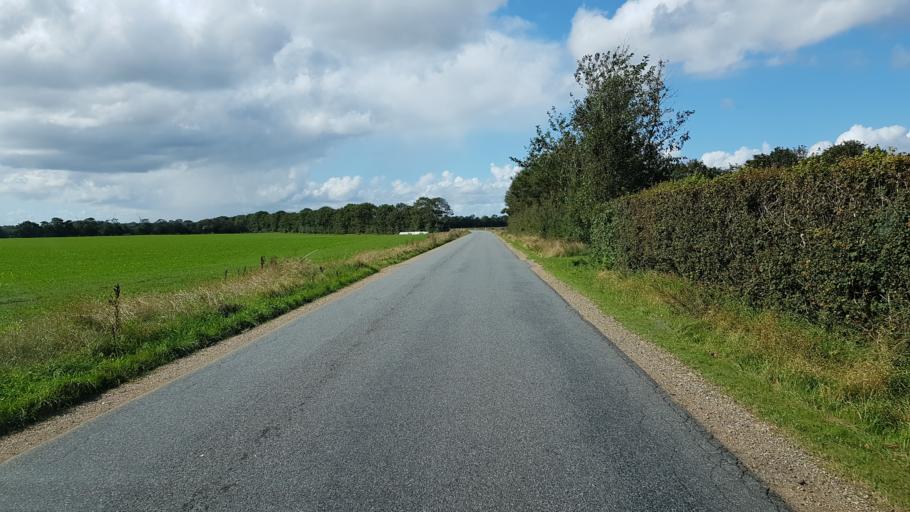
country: DK
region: South Denmark
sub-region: Esbjerg Kommune
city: Bramming
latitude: 55.6164
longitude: 8.7410
